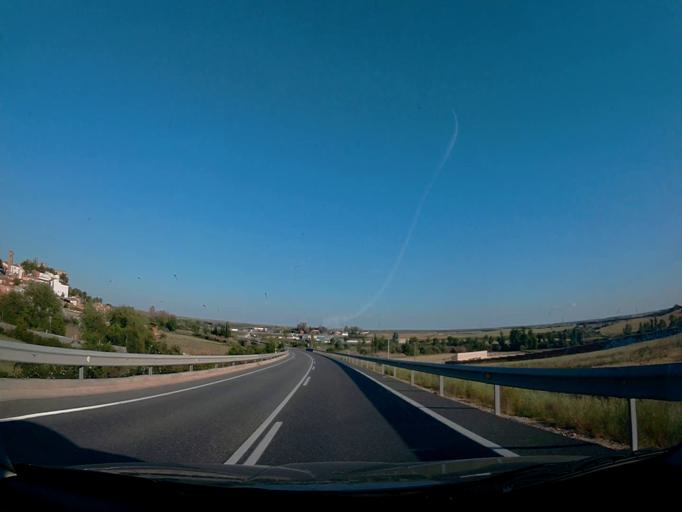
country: ES
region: Castille-La Mancha
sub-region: Province of Toledo
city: Maqueda
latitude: 40.0653
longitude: -4.3764
